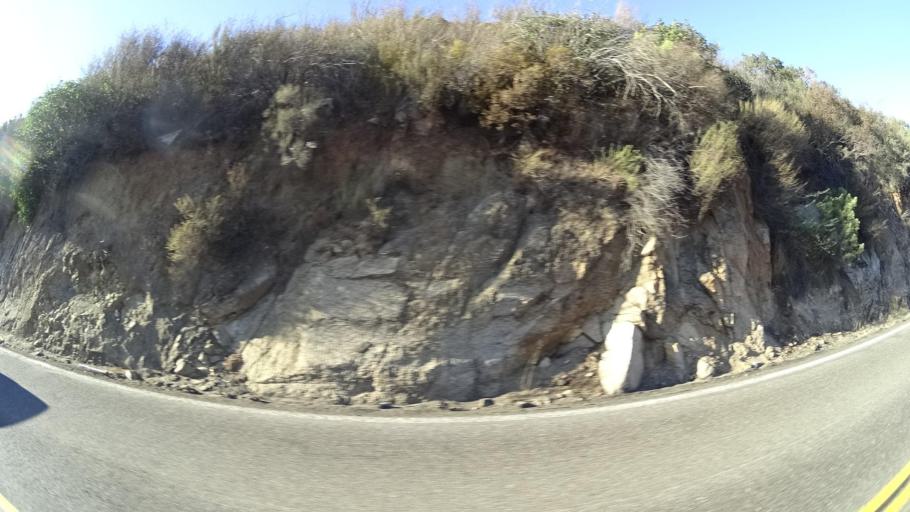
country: MX
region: Baja California
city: Tecate
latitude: 32.5968
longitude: -116.6540
